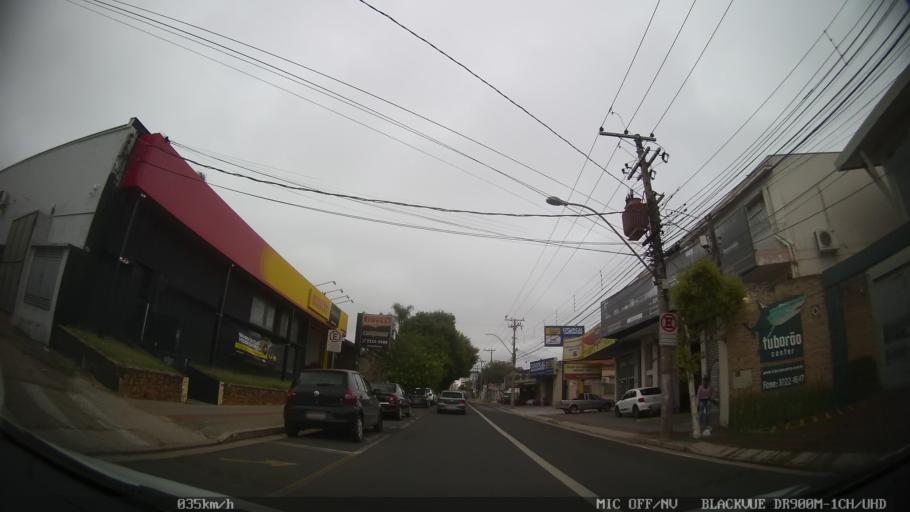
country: BR
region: Sao Paulo
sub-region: Sao Jose Do Rio Preto
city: Sao Jose do Rio Preto
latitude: -20.8221
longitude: -49.3935
